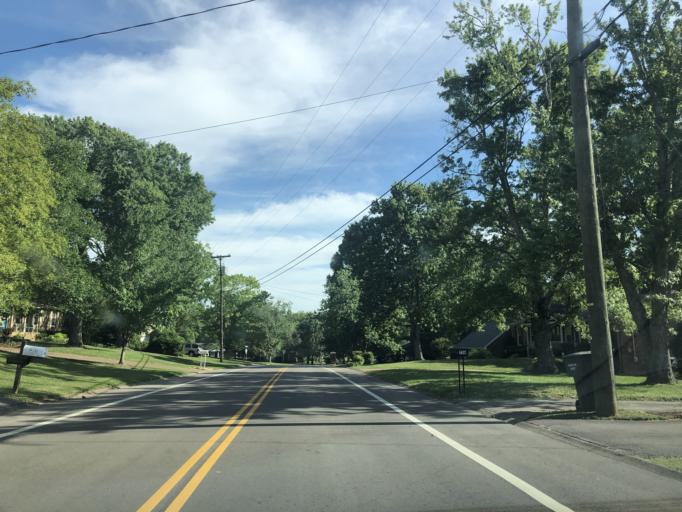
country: US
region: Tennessee
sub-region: Davidson County
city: Belle Meade
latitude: 36.0567
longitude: -86.9368
